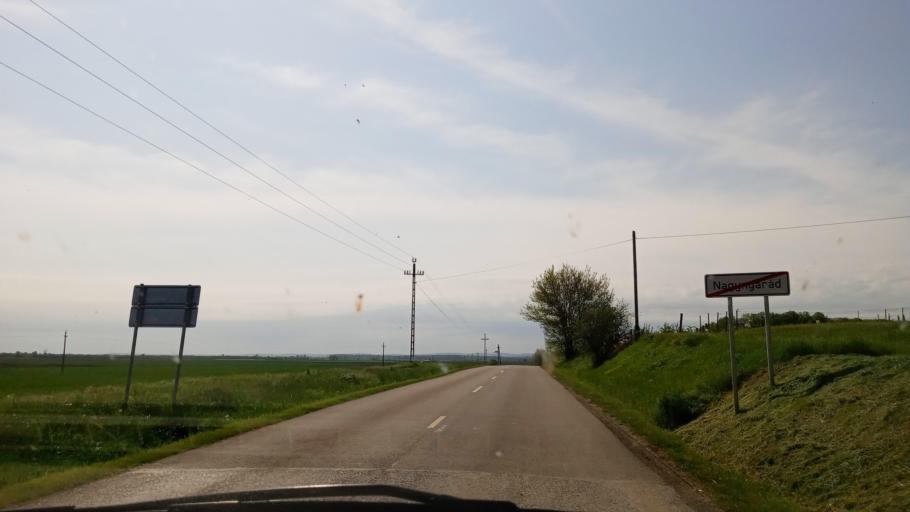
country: HU
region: Baranya
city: Boly
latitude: 45.9460
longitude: 18.5849
